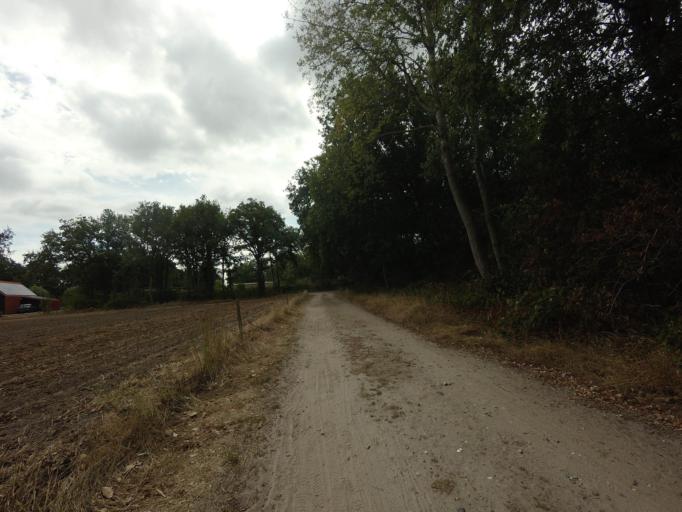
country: NL
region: North Brabant
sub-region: Gemeente Landerd
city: Zeeland
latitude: 51.6985
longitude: 5.6535
